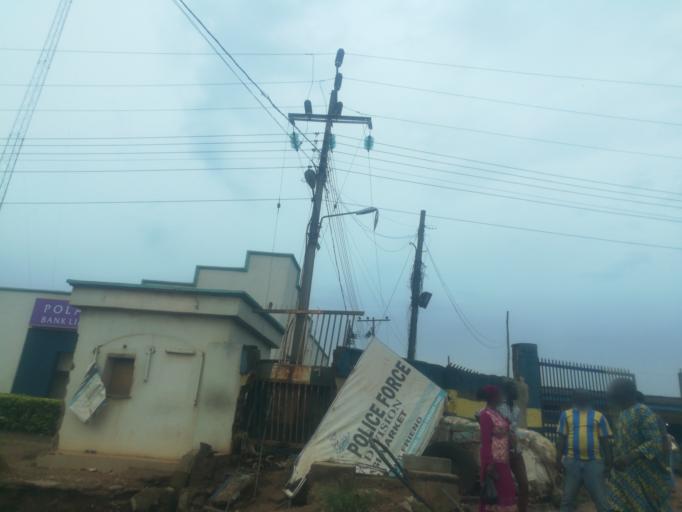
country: NG
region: Oyo
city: Ibadan
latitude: 7.3910
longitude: 3.9554
